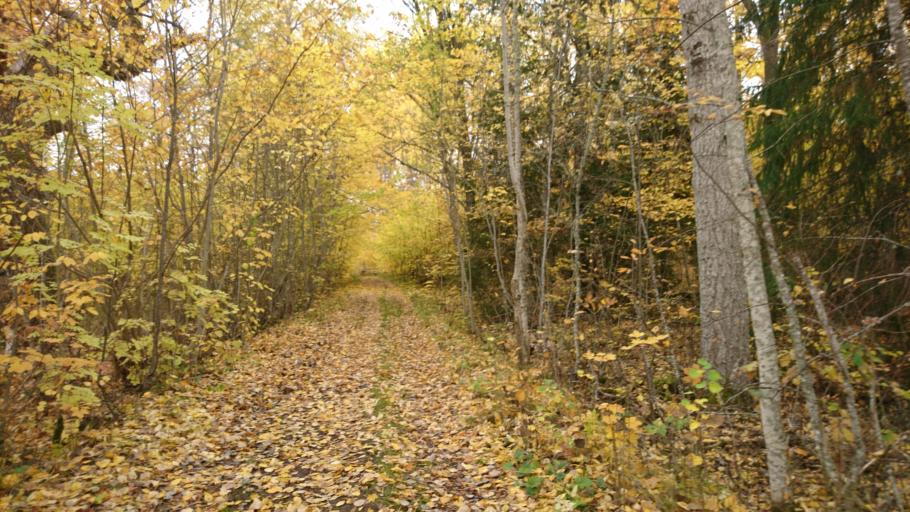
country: SE
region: Uppsala
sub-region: Knivsta Kommun
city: Knivsta
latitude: 59.8692
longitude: 17.9557
